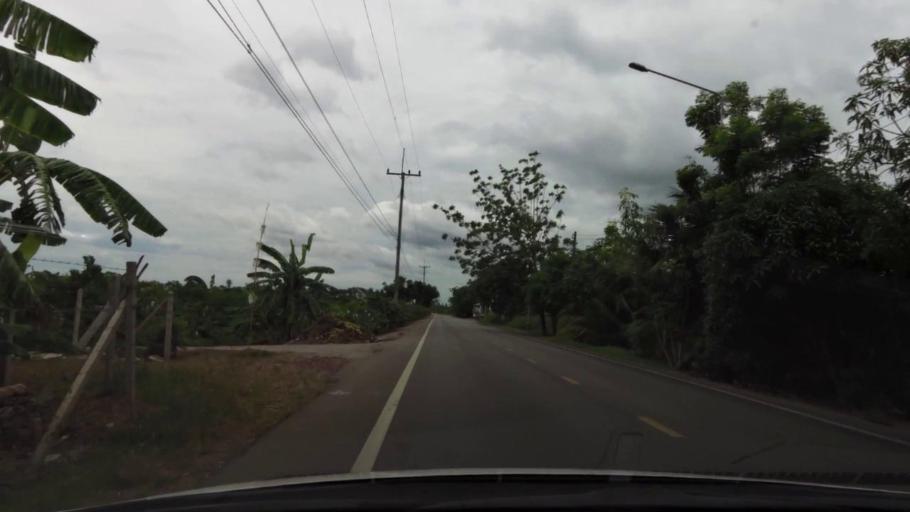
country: TH
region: Ratchaburi
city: Damnoen Saduak
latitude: 13.5621
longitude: 100.0131
